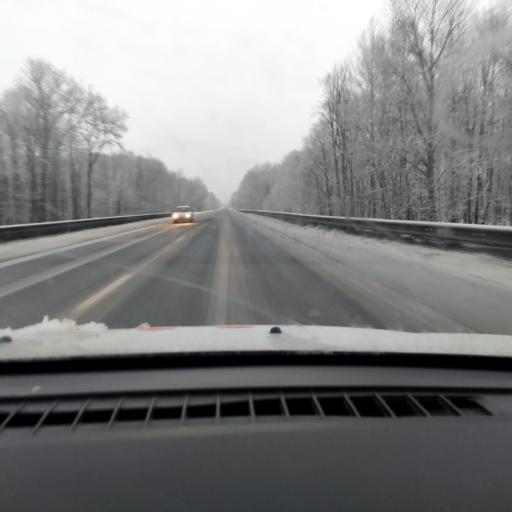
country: RU
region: Bashkortostan
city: Ulu-Telyak
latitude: 54.8316
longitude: 56.9525
